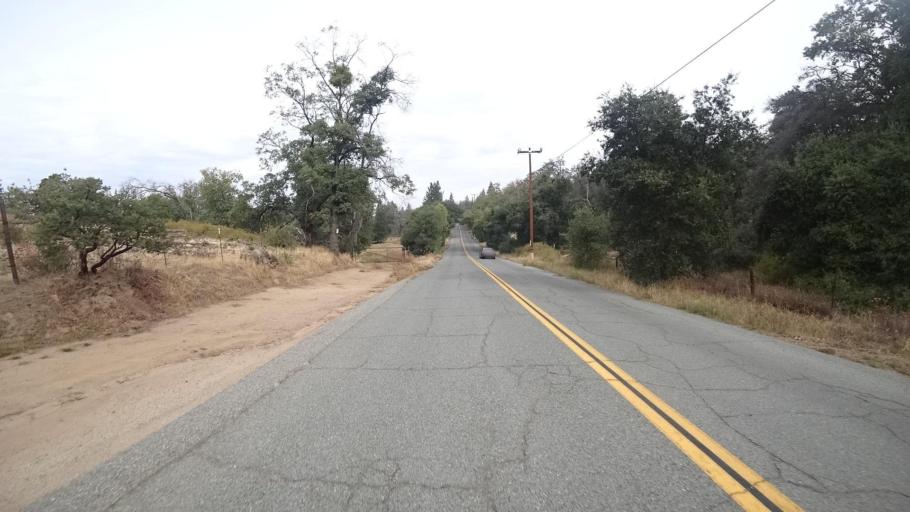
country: US
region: California
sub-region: San Diego County
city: Julian
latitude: 33.0487
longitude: -116.6013
